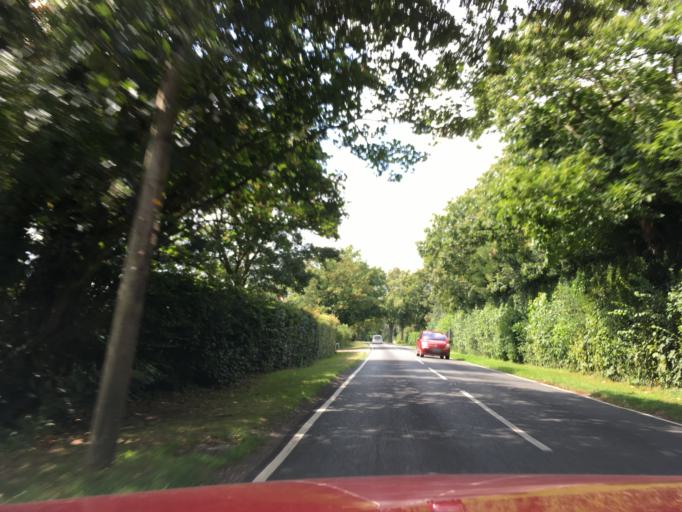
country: GB
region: England
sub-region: Kent
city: Tenterden
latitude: 51.0652
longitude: 0.7115
